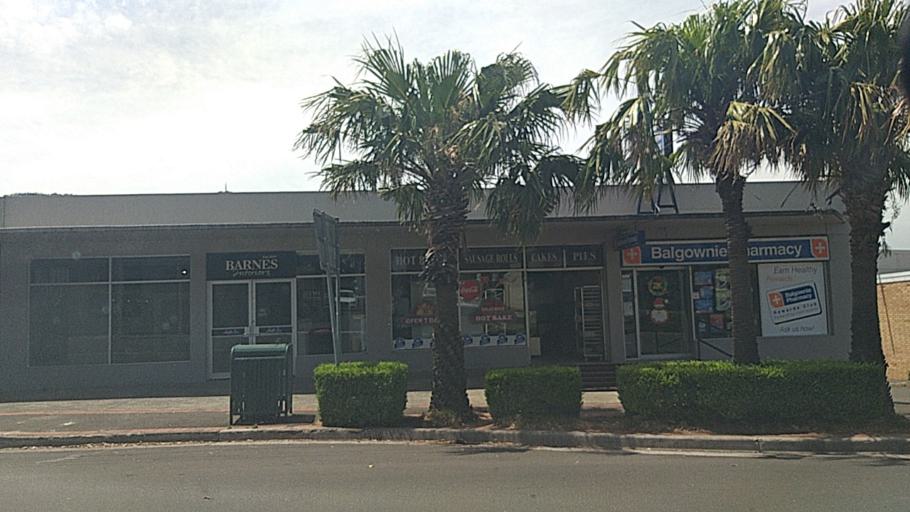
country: AU
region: New South Wales
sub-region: Wollongong
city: Mount Ousley
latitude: -34.3885
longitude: 150.8775
